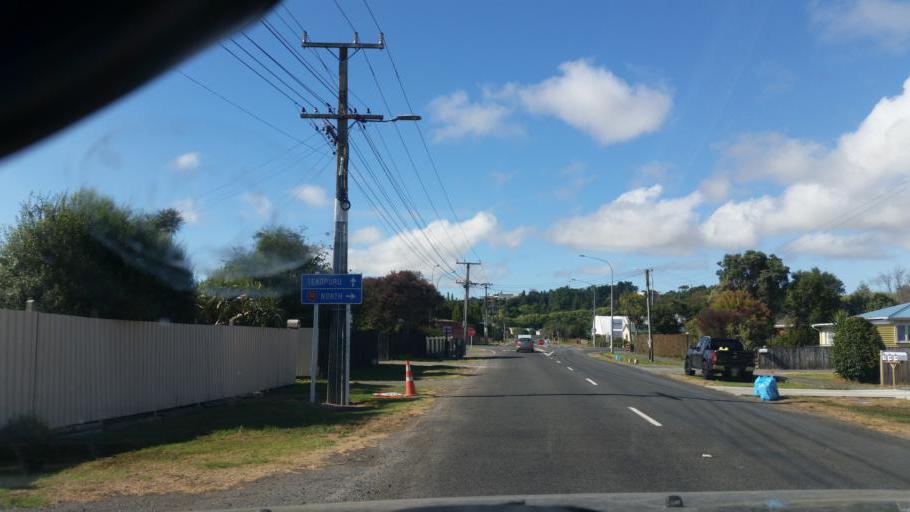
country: NZ
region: Northland
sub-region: Kaipara District
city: Dargaville
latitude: -35.9503
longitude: 173.8628
